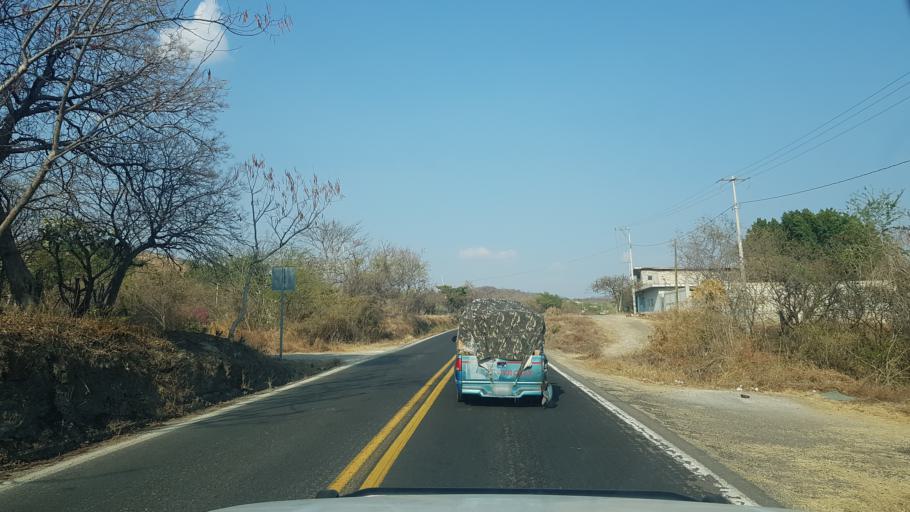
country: MX
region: Puebla
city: Calmeca
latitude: 18.6434
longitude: -98.6345
